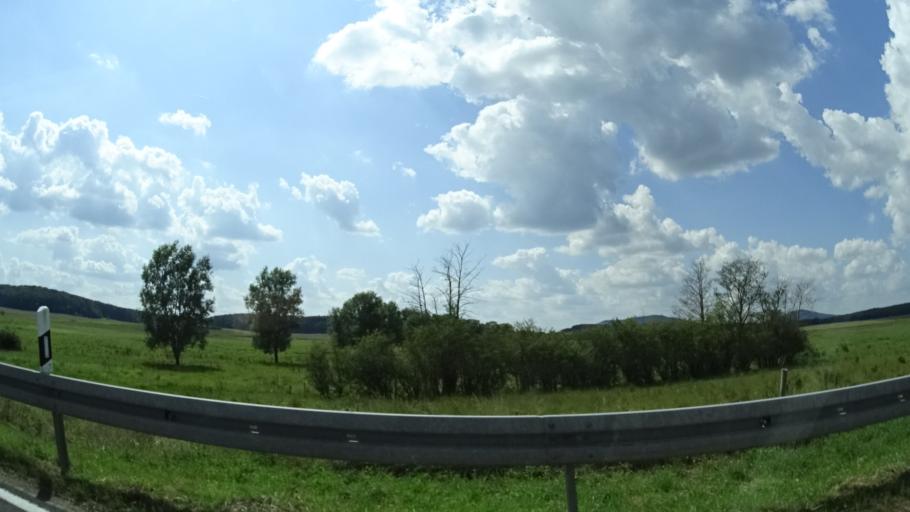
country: DE
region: Thuringia
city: Hildburghausen
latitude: 50.3749
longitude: 10.7118
